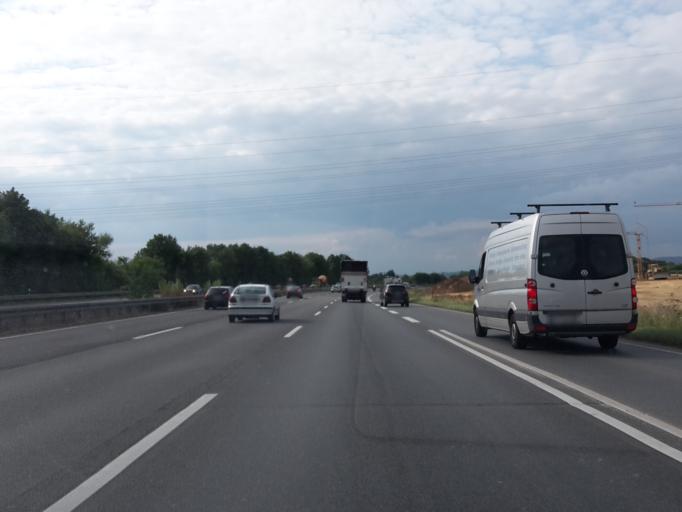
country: DE
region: Hesse
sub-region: Regierungsbezirk Giessen
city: Limburg an der Lahn
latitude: 50.3797
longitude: 8.0878
